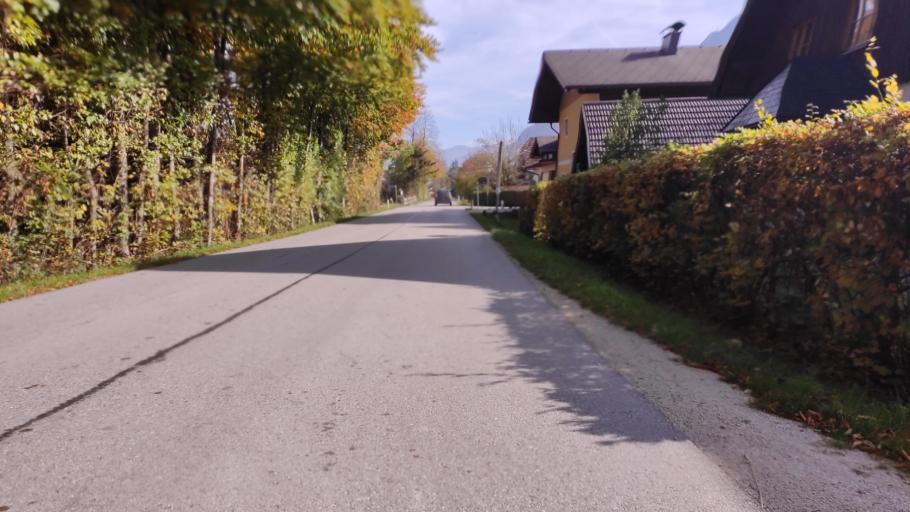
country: AT
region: Salzburg
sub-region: Politischer Bezirk Salzburg-Umgebung
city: Strobl
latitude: 47.7169
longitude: 13.5215
